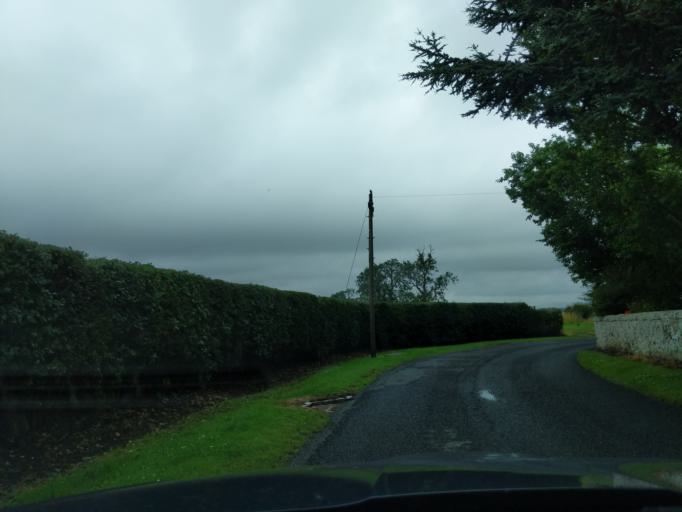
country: GB
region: England
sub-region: Northumberland
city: Ford
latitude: 55.6966
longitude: -2.1409
